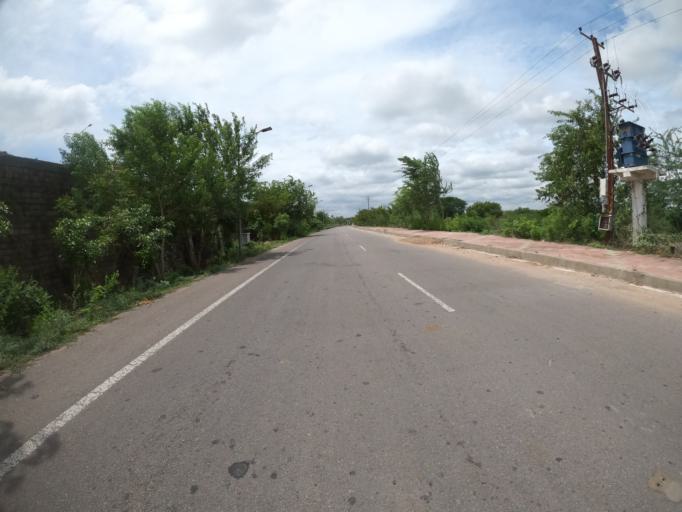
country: IN
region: Telangana
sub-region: Rangareddi
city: Balapur
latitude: 17.2859
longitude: 78.3822
